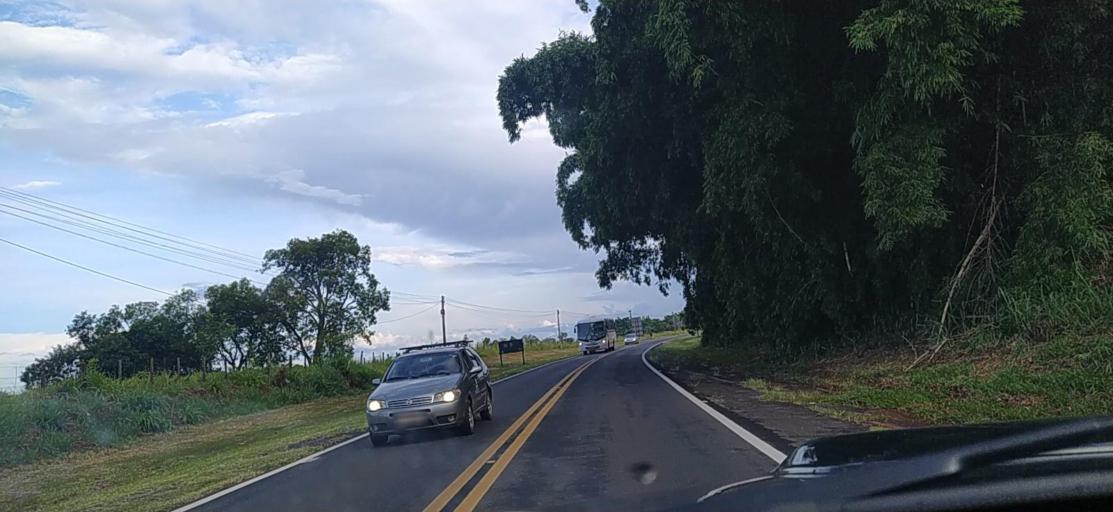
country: BR
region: Sao Paulo
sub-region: Pindorama
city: Pindorama
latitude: -21.1711
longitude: -48.9266
